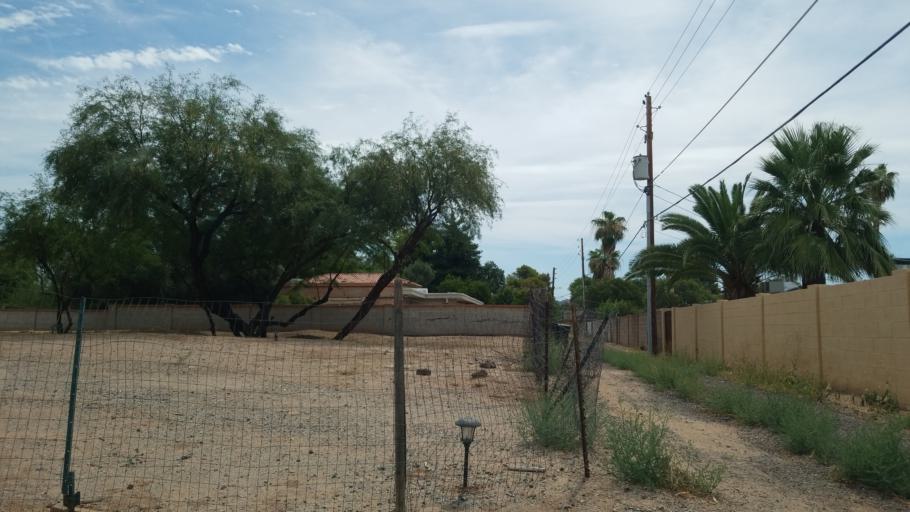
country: US
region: Arizona
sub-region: Maricopa County
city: Glendale
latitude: 33.5567
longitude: -112.0956
